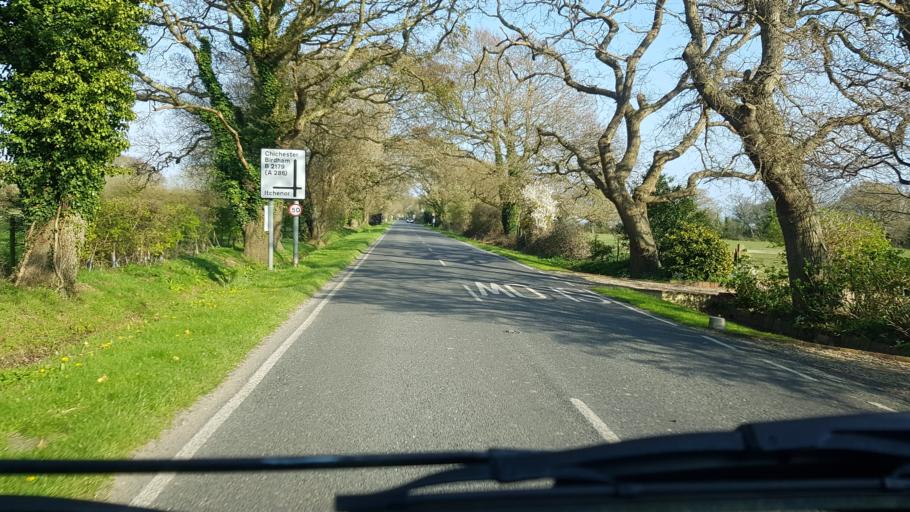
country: GB
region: England
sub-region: West Sussex
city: East Wittering
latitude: 50.7872
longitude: -0.8677
